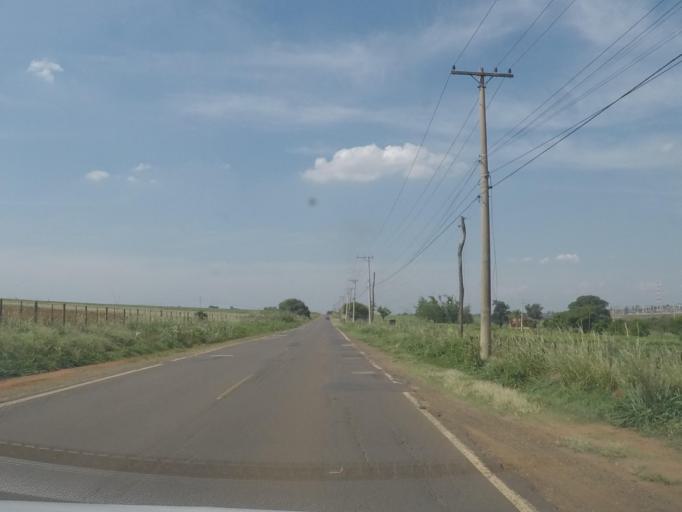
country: BR
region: Sao Paulo
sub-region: Sumare
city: Sumare
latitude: -22.8758
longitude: -47.3000
